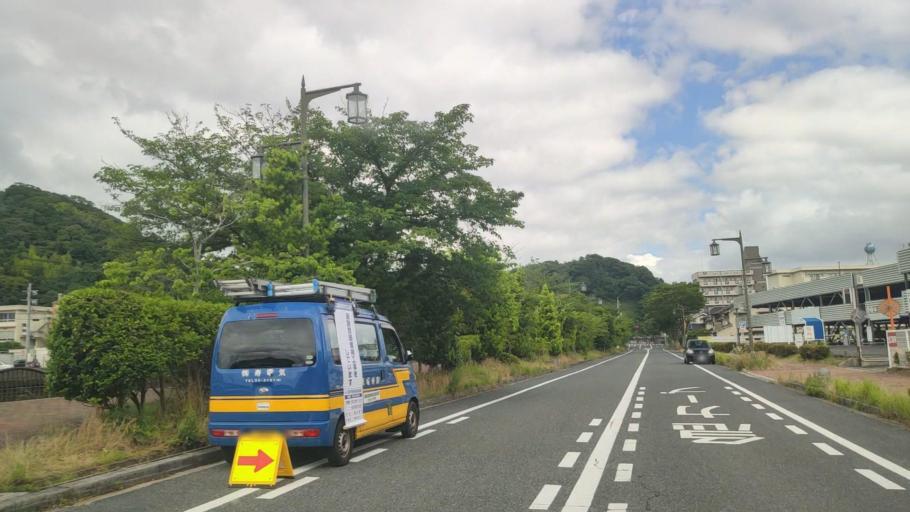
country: JP
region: Tottori
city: Yonago
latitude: 35.4213
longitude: 133.3321
